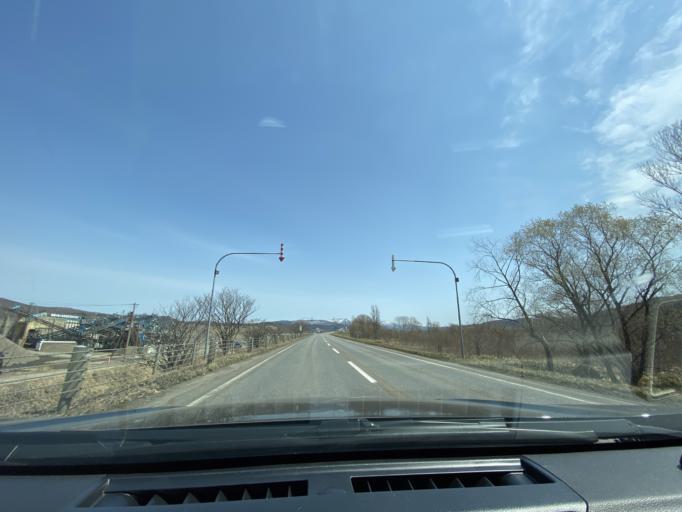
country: JP
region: Hokkaido
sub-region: Asahikawa-shi
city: Asahikawa
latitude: 43.8985
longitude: 142.5303
